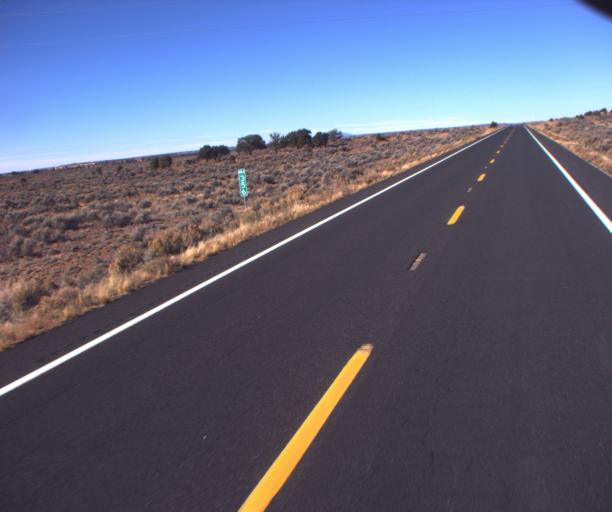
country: US
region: Arizona
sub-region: Coconino County
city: Kaibito
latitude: 36.5391
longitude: -110.7011
